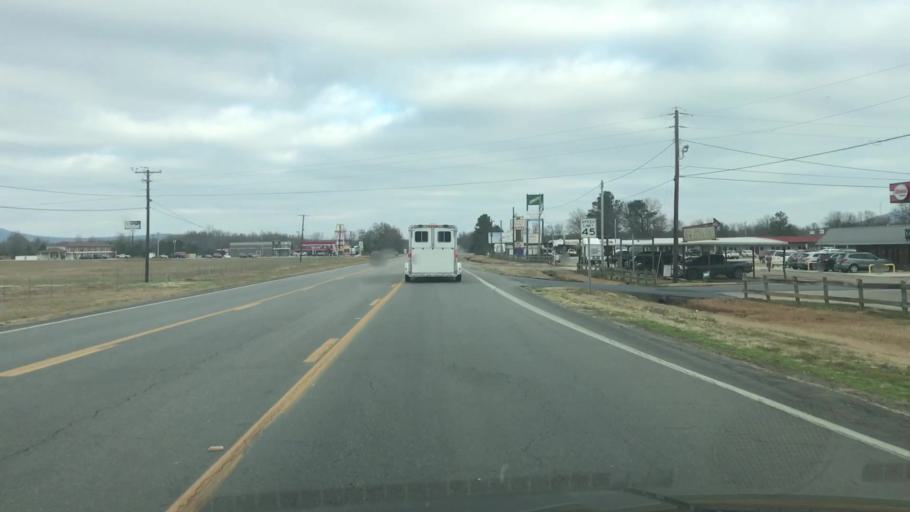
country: US
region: Arkansas
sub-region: Scott County
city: Waldron
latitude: 34.9011
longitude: -94.1074
